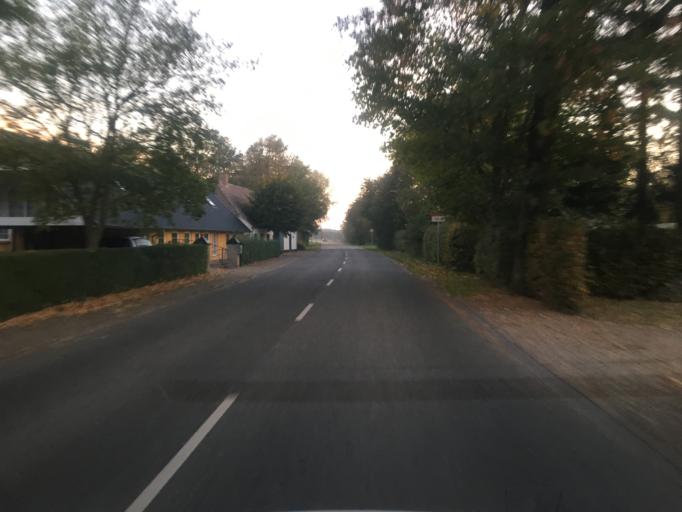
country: DE
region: Schleswig-Holstein
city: Bramstedtlund
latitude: 54.9534
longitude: 9.1062
